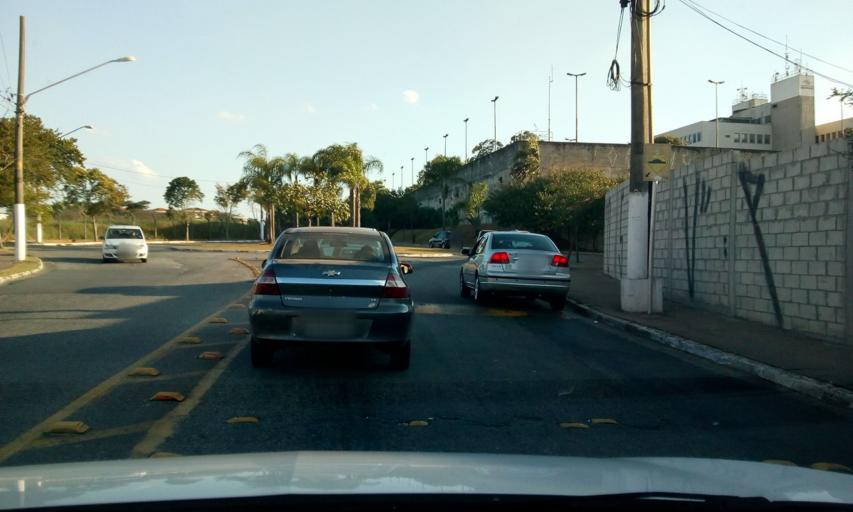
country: BR
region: Sao Paulo
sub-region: Diadema
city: Diadema
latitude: -23.6800
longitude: -46.6745
